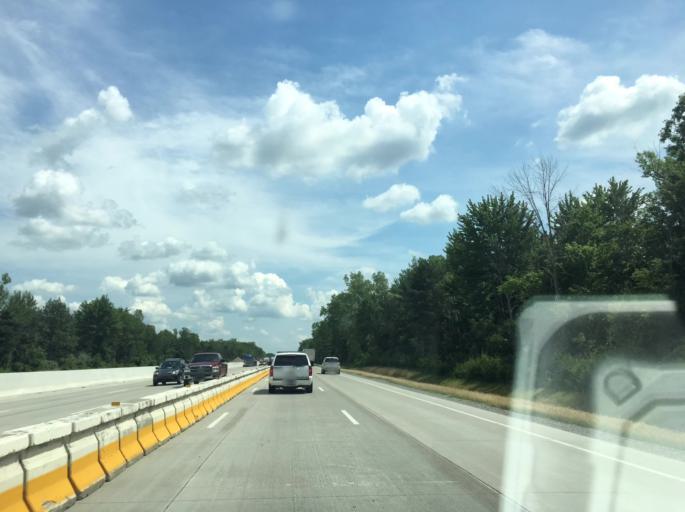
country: US
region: Michigan
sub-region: Saginaw County
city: Bridgeport
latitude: 43.3853
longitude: -83.8814
